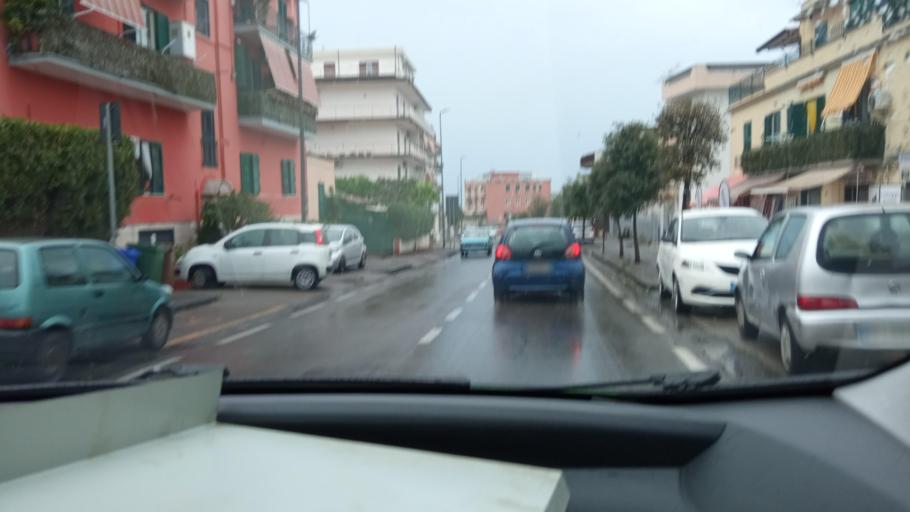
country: IT
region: Campania
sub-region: Provincia di Napoli
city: Pozzuoli
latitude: 40.8332
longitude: 14.1160
